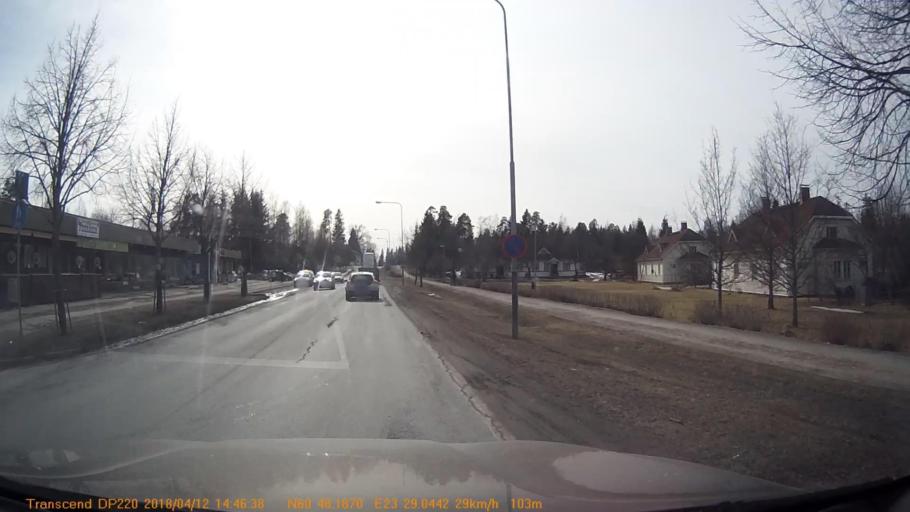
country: FI
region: Haeme
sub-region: Forssa
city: Jokioinen
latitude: 60.8031
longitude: 23.4840
